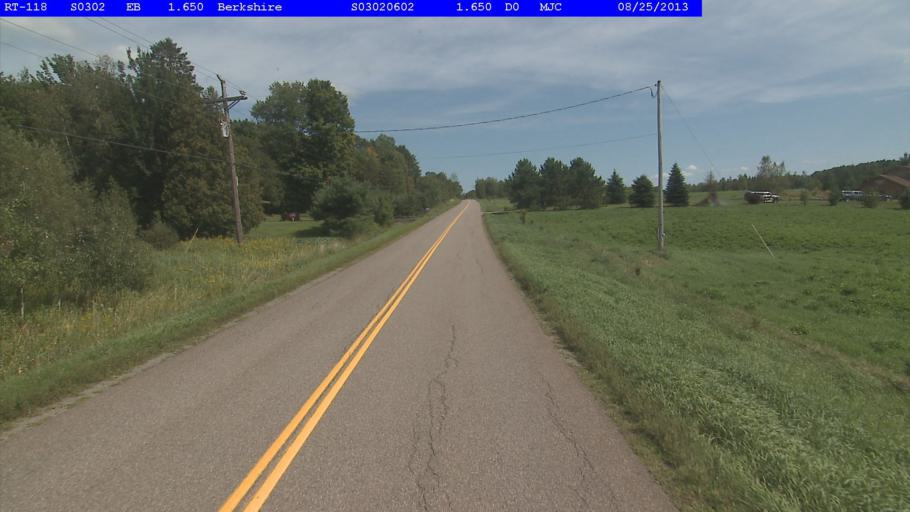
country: US
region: Vermont
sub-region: Franklin County
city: Enosburg Falls
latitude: 44.9792
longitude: -72.7840
